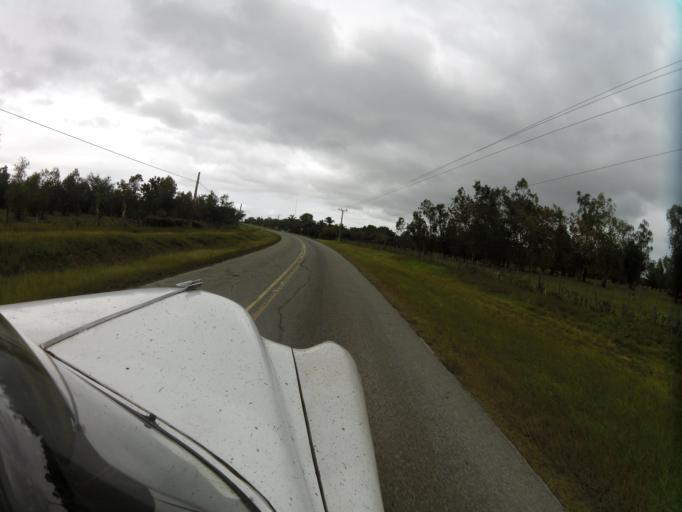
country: CU
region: Las Tunas
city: Las Tunas
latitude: 20.9272
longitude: -76.9006
